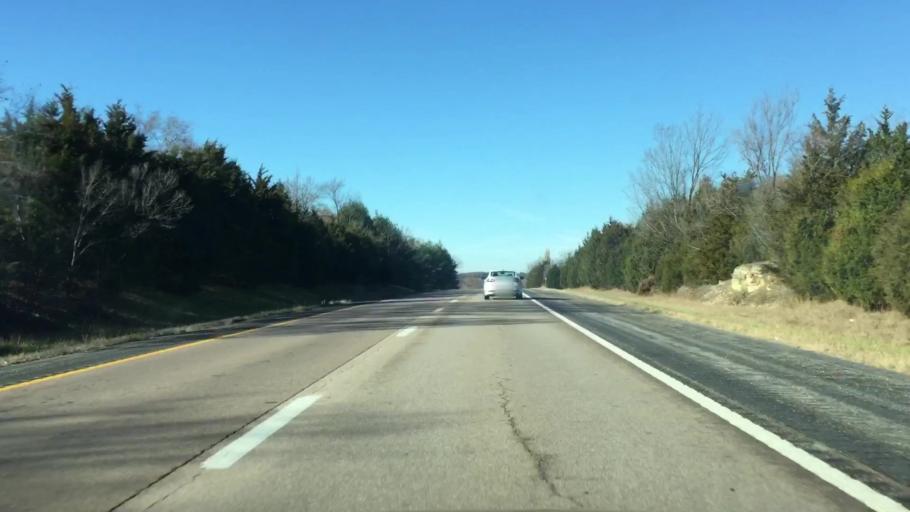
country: US
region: Missouri
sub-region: Miller County
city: Eldon
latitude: 38.3681
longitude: -92.4752
